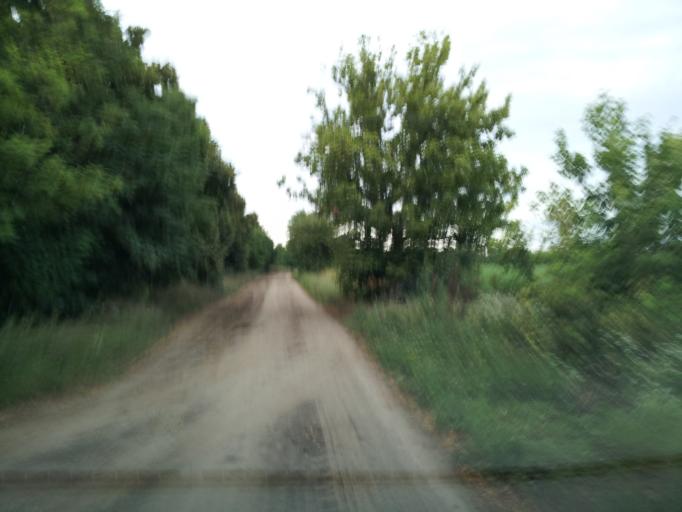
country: HU
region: Fejer
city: Lajoskomarom
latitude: 46.8134
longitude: 18.2755
